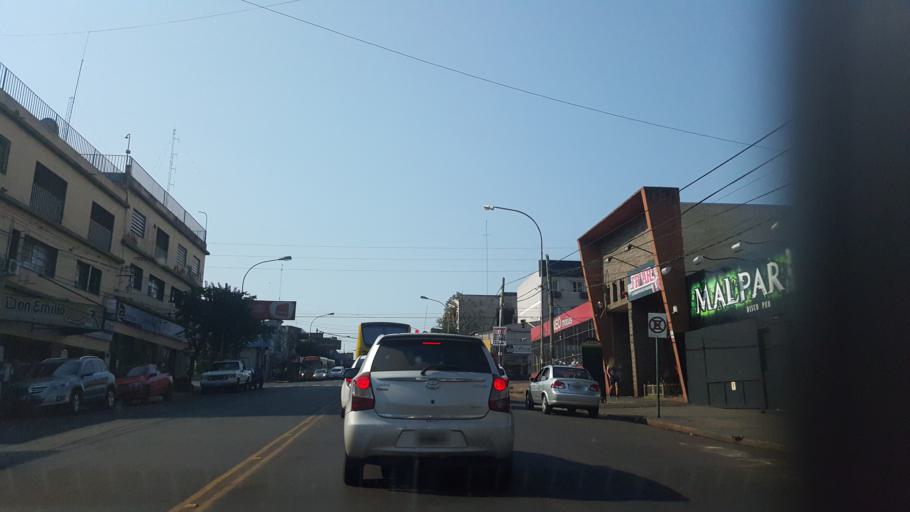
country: AR
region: Misiones
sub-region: Departamento de Capital
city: Posadas
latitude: -27.3783
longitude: -55.8991
